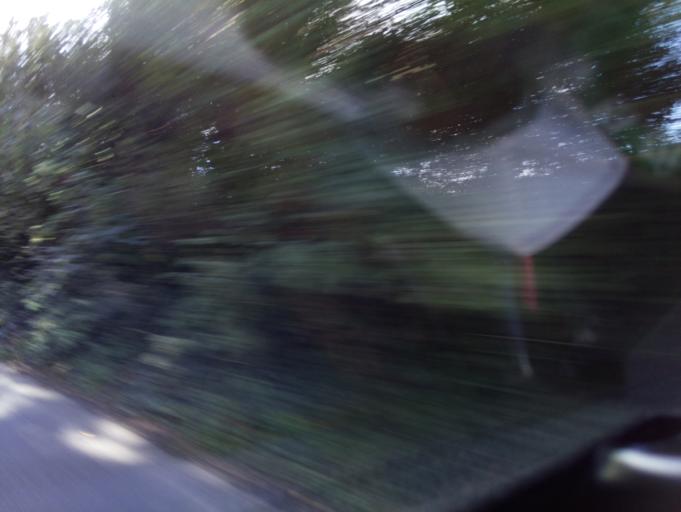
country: GB
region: England
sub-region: Devon
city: Buckfastleigh
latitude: 50.4329
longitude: -3.7550
